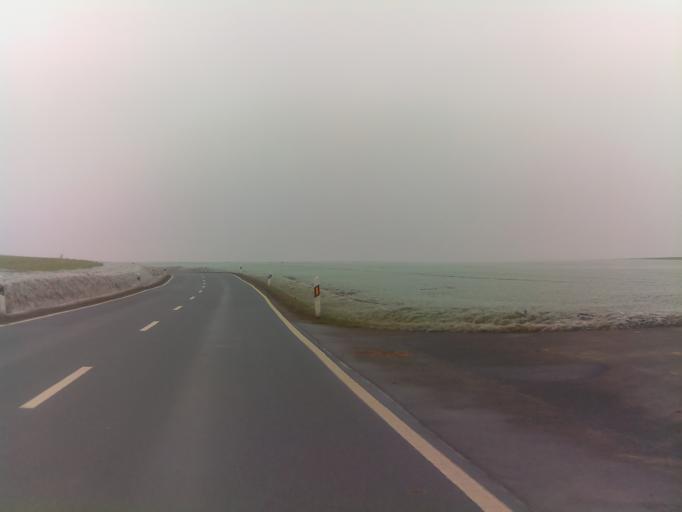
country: DE
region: Bavaria
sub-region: Regierungsbezirk Unterfranken
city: Gaukonigshofen
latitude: 49.6395
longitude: 10.0171
